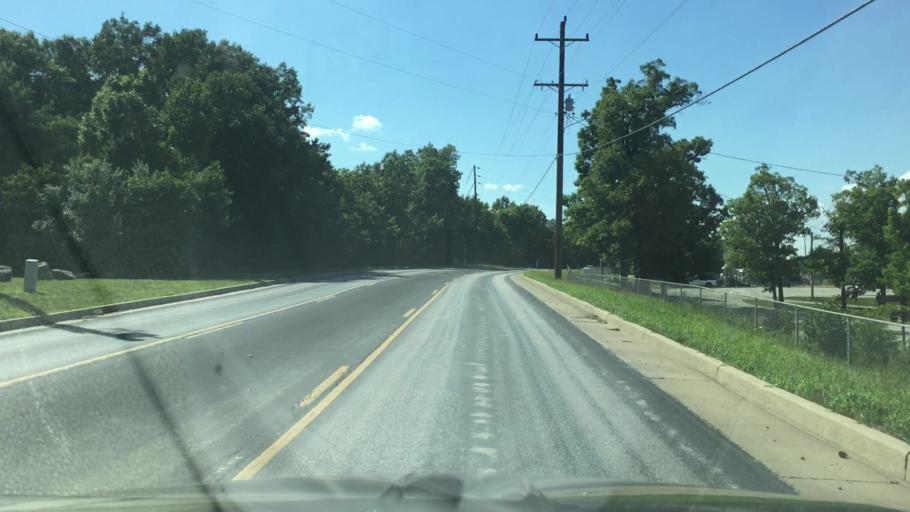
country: US
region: Missouri
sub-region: Camden County
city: Osage Beach
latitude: 38.1489
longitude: -92.5978
